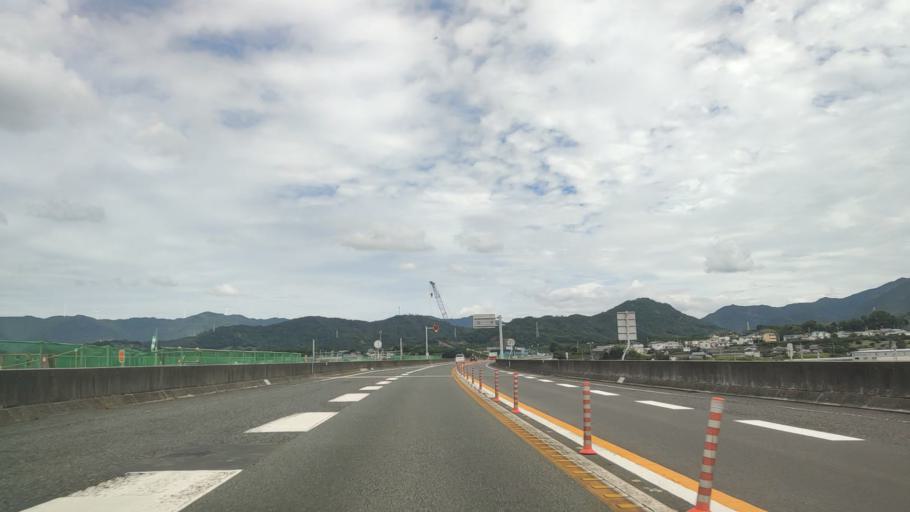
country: JP
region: Wakayama
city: Gobo
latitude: 33.9014
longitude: 135.1865
